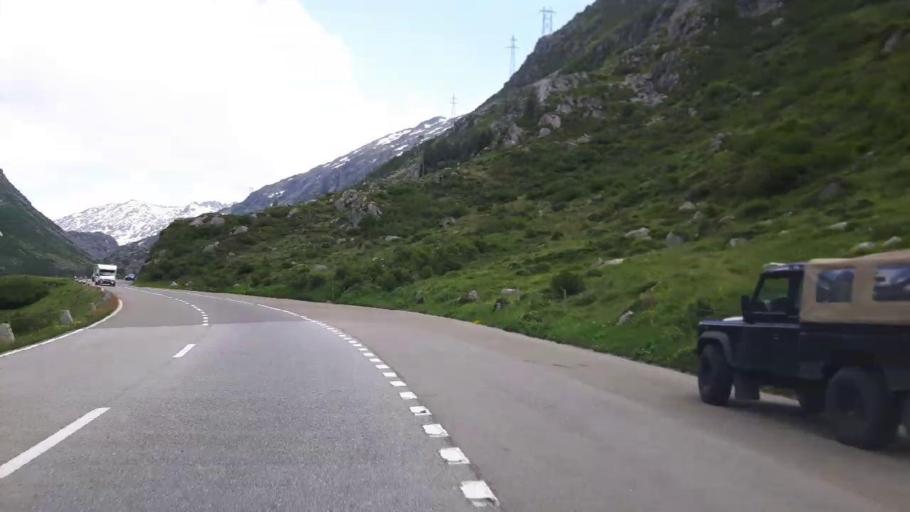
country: CH
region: Uri
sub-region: Uri
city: Andermatt
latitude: 46.6059
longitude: 8.5659
